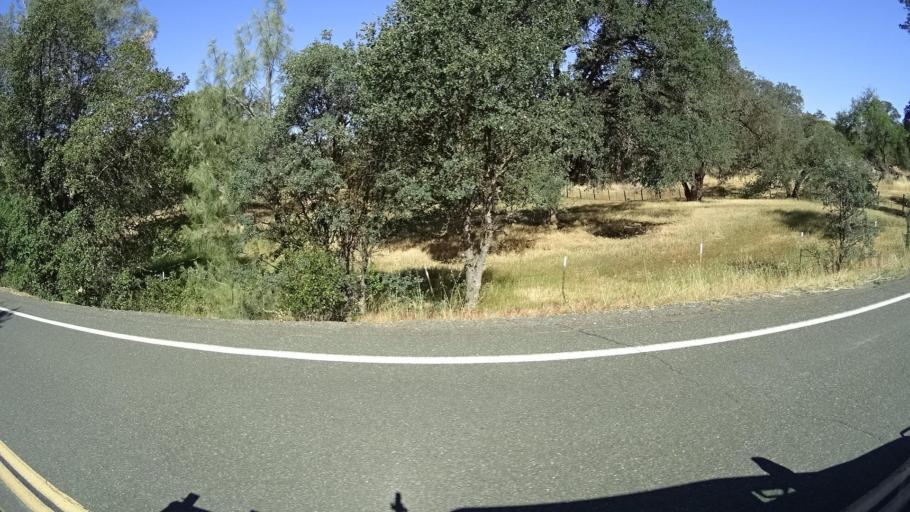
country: US
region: California
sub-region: Lake County
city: Clearlake Oaks
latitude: 39.0095
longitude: -122.6498
